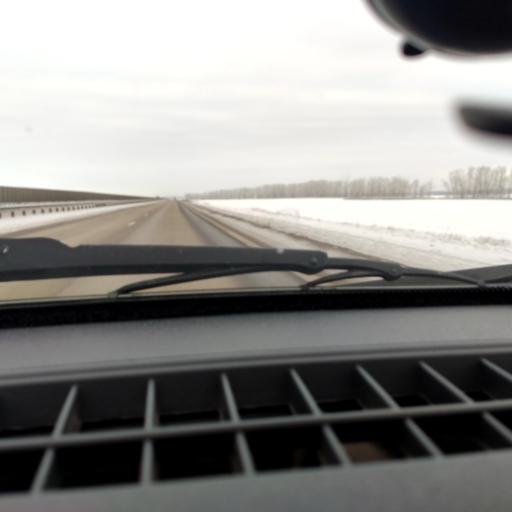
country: RU
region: Bashkortostan
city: Kushnarenkovo
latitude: 55.0901
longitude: 55.2524
